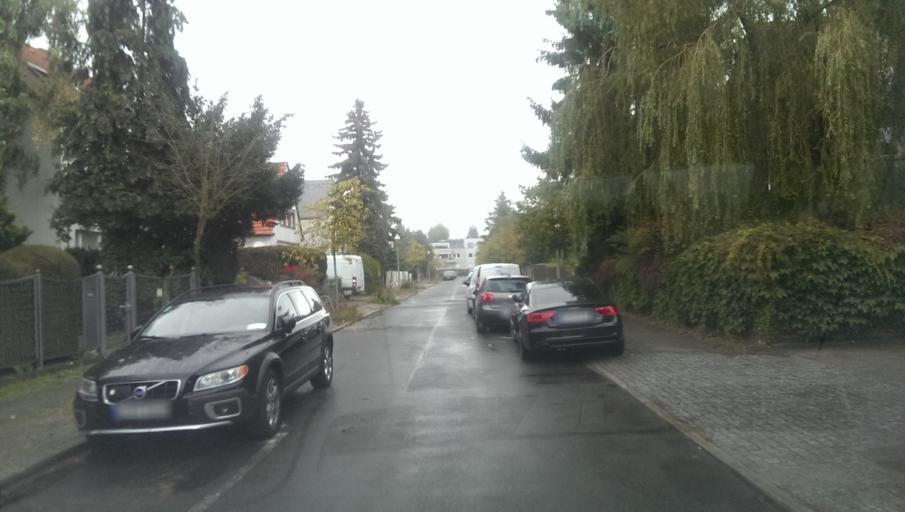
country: DE
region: Berlin
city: Zehlendorf Bezirk
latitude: 52.4293
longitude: 13.2683
